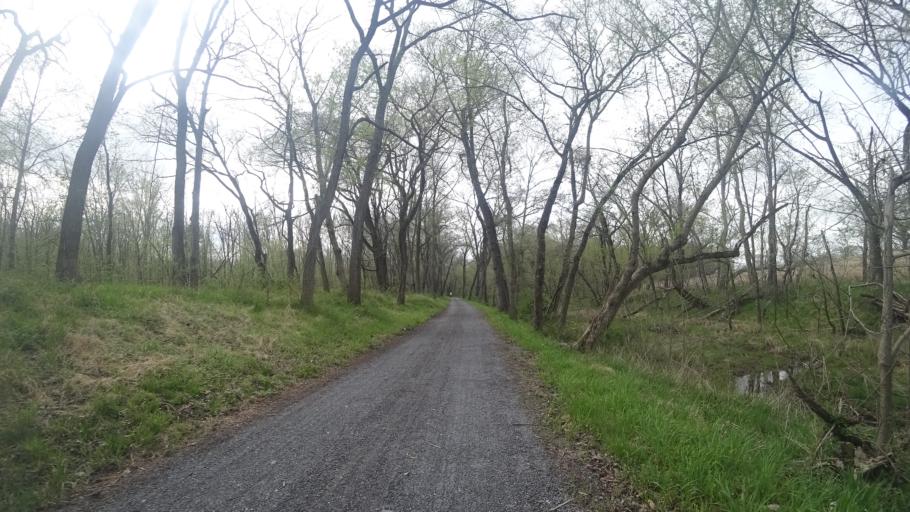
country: US
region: Virginia
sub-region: Loudoun County
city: Belmont
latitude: 39.1177
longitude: -77.4883
